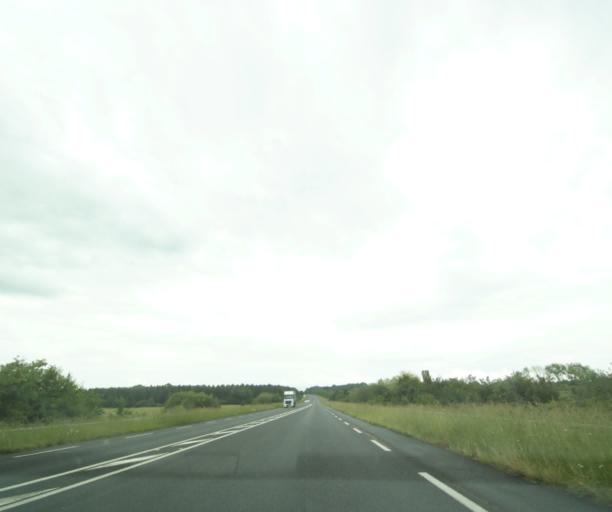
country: FR
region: Poitou-Charentes
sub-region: Departement des Deux-Sevres
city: Airvault
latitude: 46.7858
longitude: -0.2161
